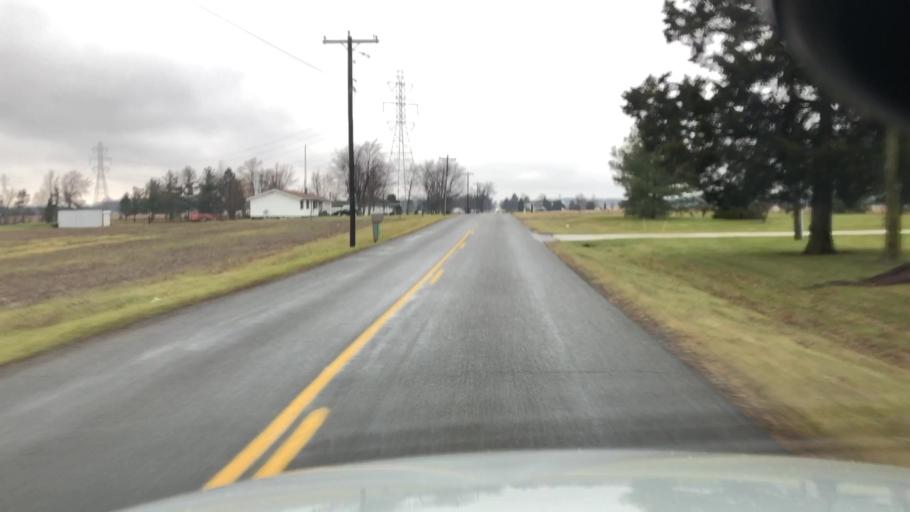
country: US
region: Ohio
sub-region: Allen County
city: Lima
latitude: 40.7753
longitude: -84.0131
